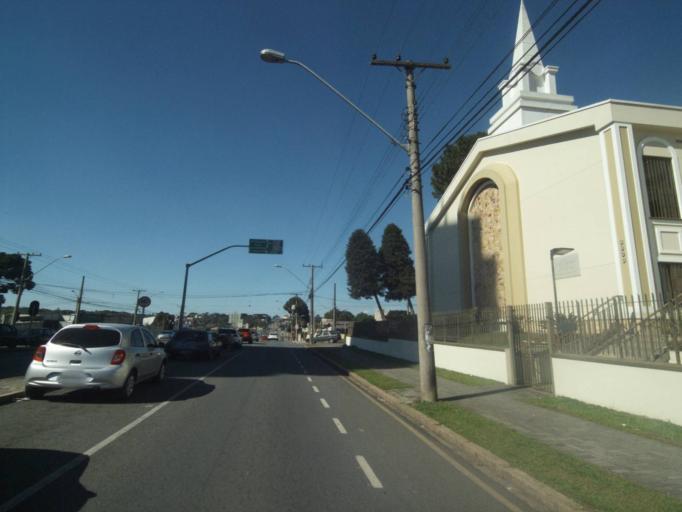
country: BR
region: Parana
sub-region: Curitiba
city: Curitiba
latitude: -25.3841
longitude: -49.2317
